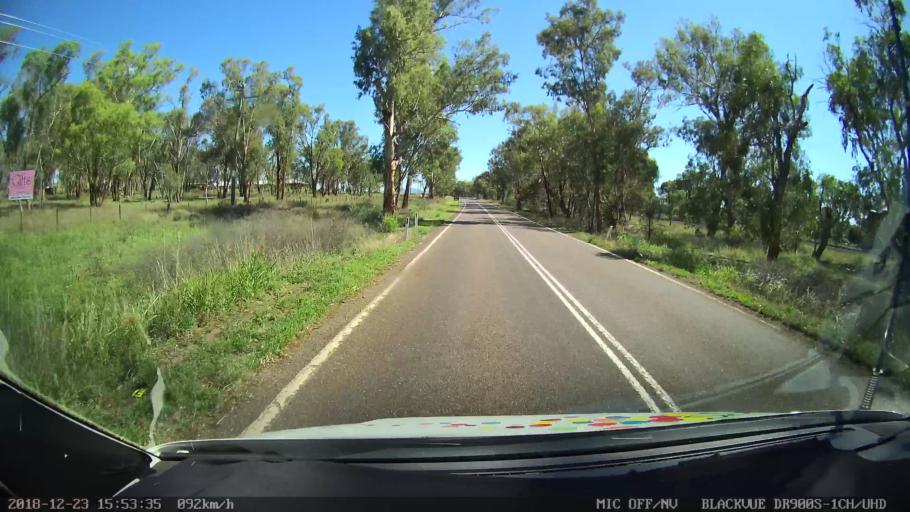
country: AU
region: New South Wales
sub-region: Tamworth Municipality
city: Phillip
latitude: -31.1351
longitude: 150.8800
